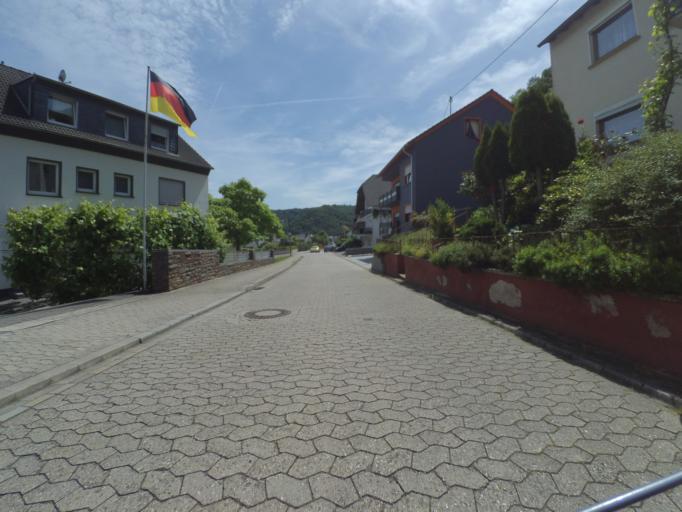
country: DE
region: Rheinland-Pfalz
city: Kobern-Gondorf
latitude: 50.2986
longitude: 7.4589
